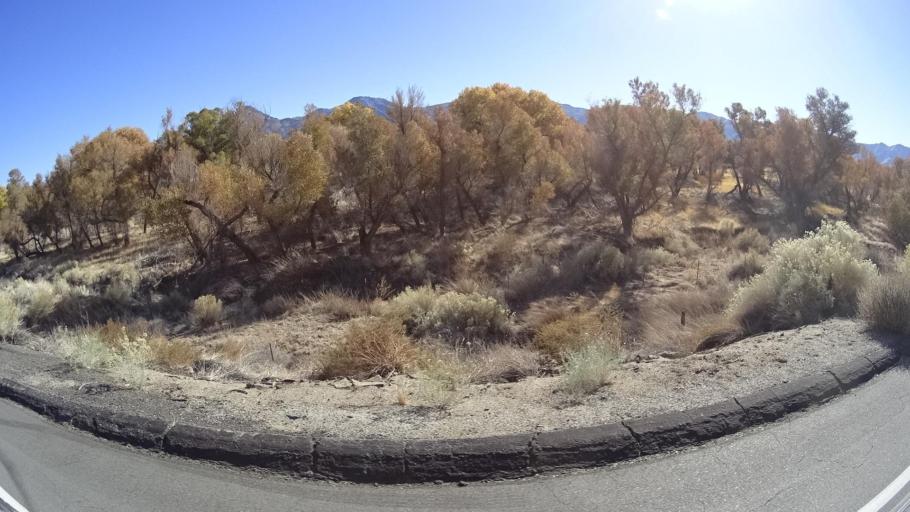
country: US
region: California
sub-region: Kern County
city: Weldon
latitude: 35.6731
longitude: -118.3437
